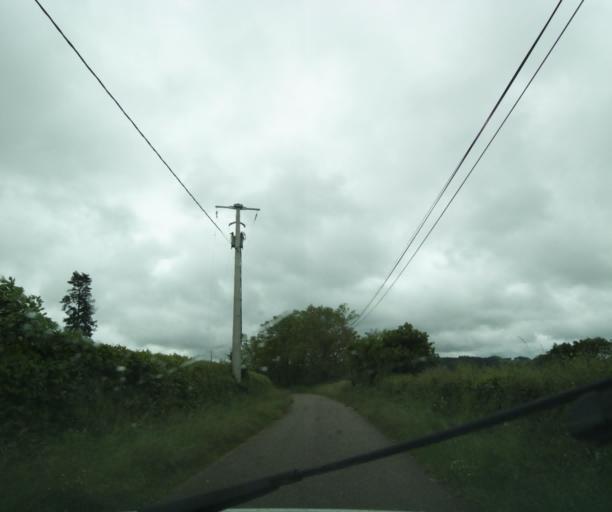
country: FR
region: Bourgogne
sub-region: Departement de Saone-et-Loire
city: Matour
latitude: 46.4581
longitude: 4.4515
